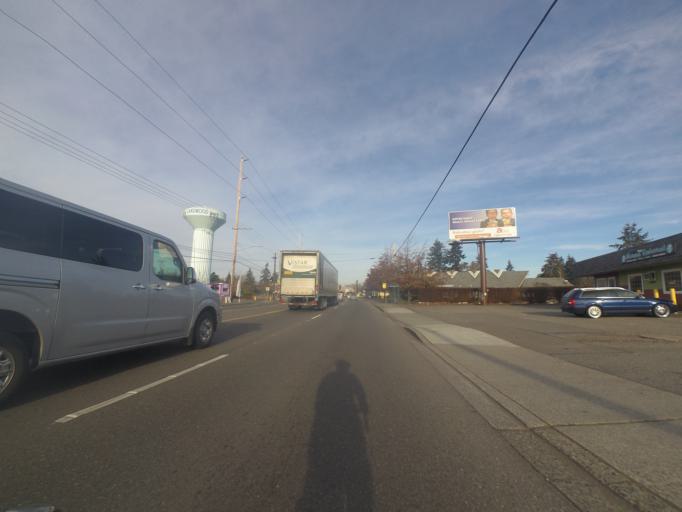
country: US
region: Washington
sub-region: Pierce County
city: Lakewood
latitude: 47.1618
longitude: -122.5052
